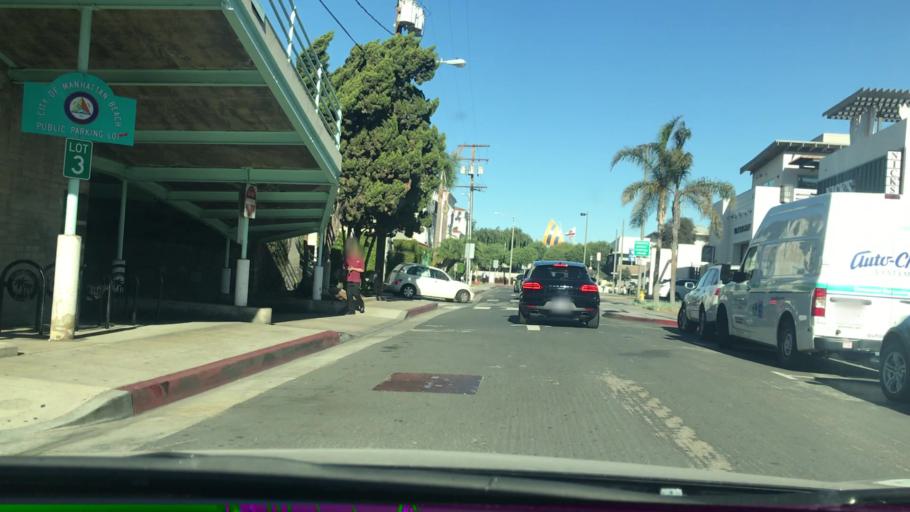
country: US
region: California
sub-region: Los Angeles County
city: Manhattan Beach
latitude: 33.8858
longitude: -118.4089
